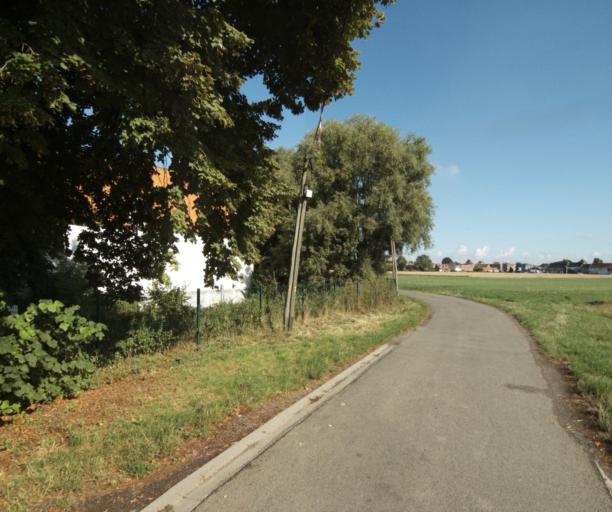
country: FR
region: Nord-Pas-de-Calais
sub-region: Departement du Nord
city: Toufflers
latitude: 50.6547
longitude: 3.2391
